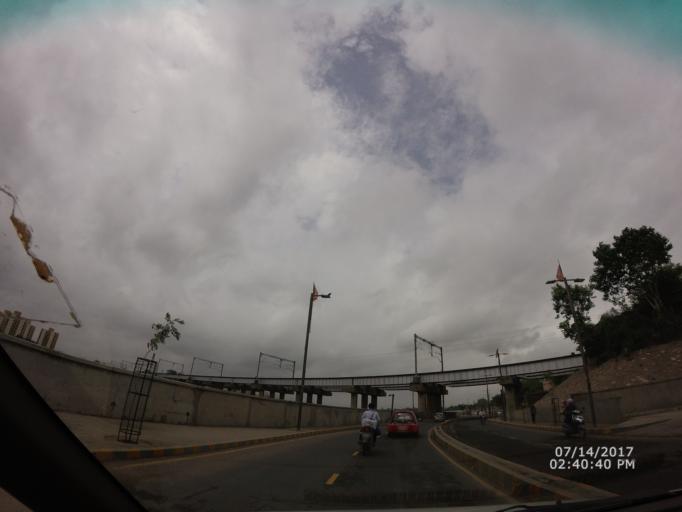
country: IN
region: Gujarat
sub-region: Ahmadabad
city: Ahmedabad
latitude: 23.0614
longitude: 72.5889
